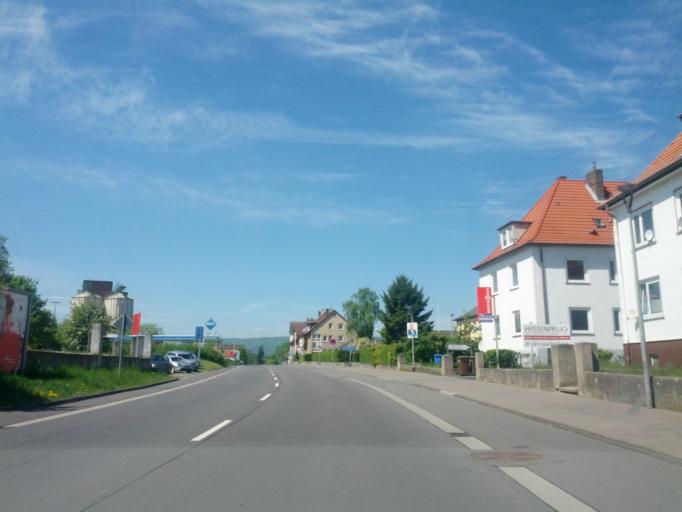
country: DE
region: Hesse
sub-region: Regierungsbezirk Kassel
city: Eschwege
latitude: 51.1930
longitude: 10.0372
